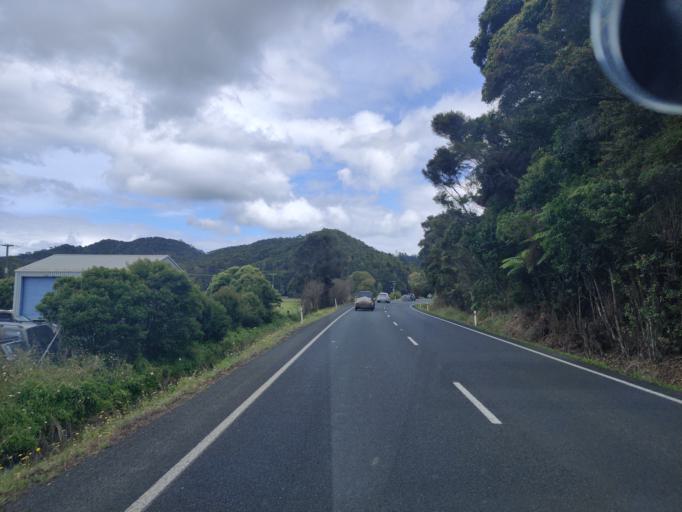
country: NZ
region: Northland
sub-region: Far North District
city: Kerikeri
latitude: -35.0926
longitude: 173.7699
